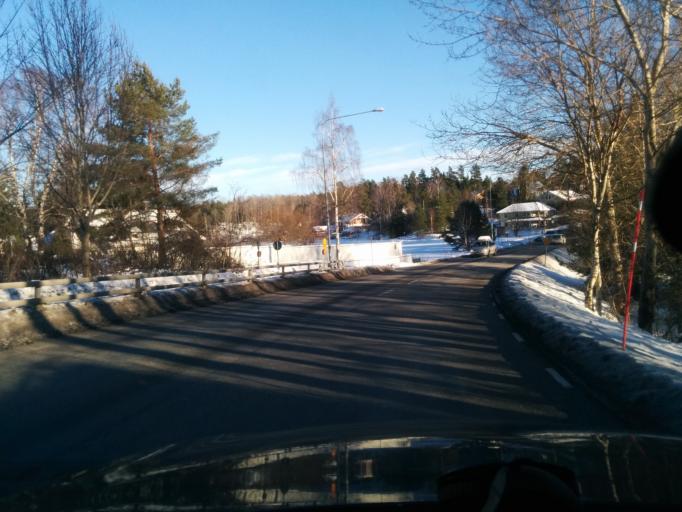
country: SE
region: Stockholm
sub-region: Taby Kommun
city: Taby
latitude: 59.4735
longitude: 18.0996
